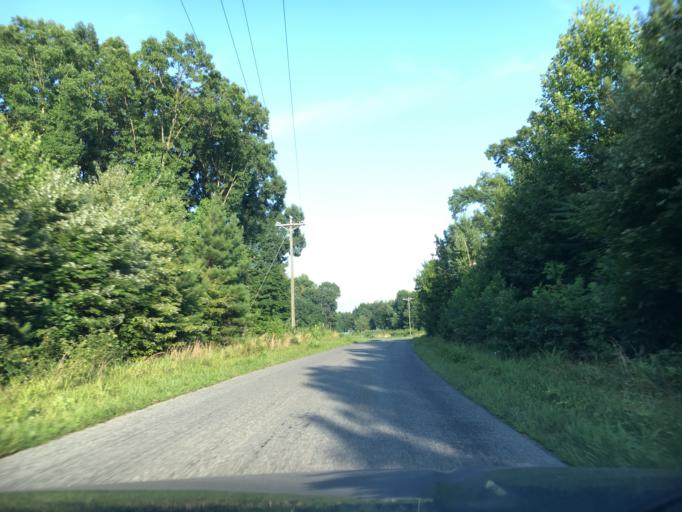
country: US
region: Virginia
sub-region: Pittsylvania County
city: Gretna
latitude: 36.8438
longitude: -79.2057
